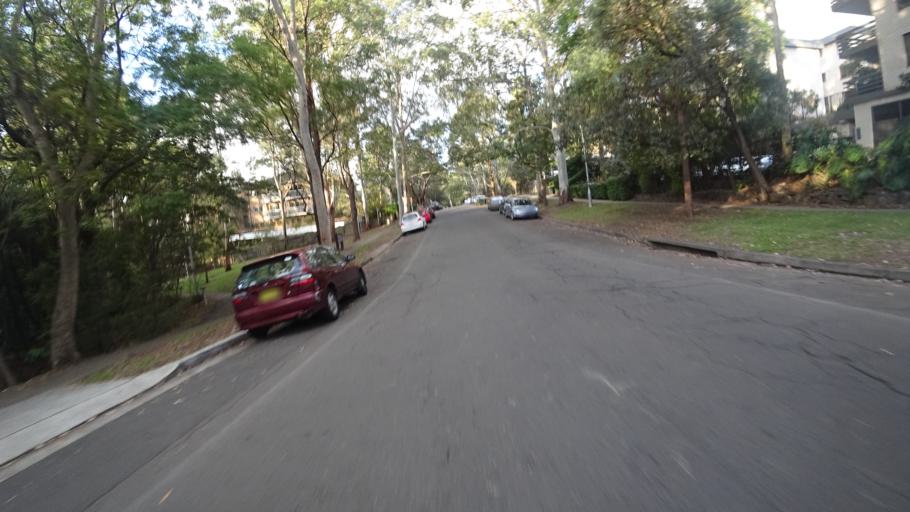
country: AU
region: New South Wales
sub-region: Willoughby
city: Lane Cove North
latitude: -33.8101
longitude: 151.1749
